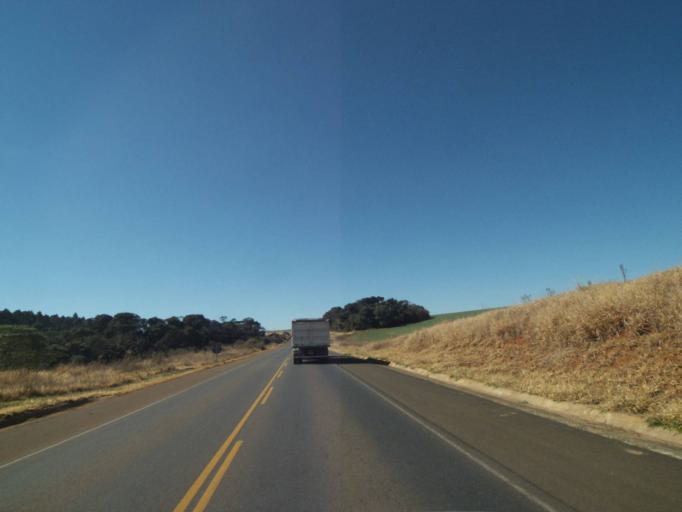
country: BR
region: Parana
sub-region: Tibagi
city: Tibagi
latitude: -24.4630
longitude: -50.4331
